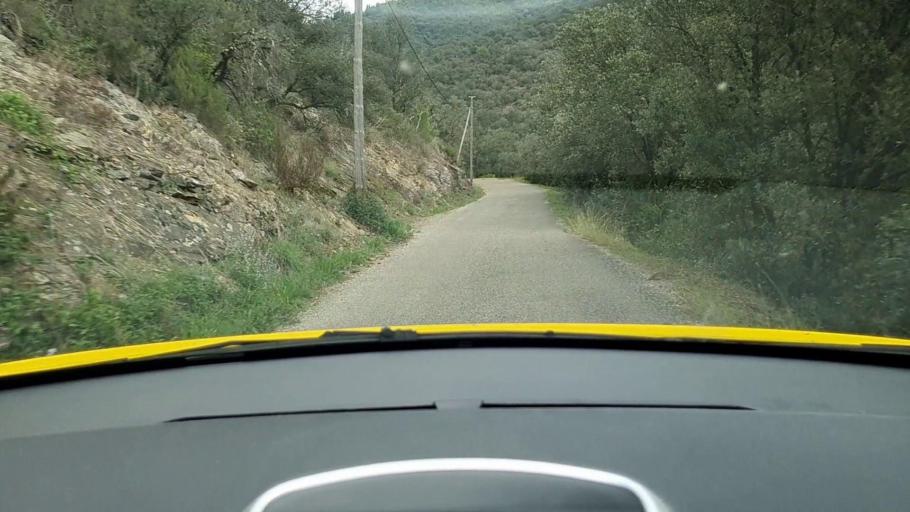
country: FR
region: Languedoc-Roussillon
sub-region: Departement du Gard
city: Sumene
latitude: 44.0128
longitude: 3.6606
